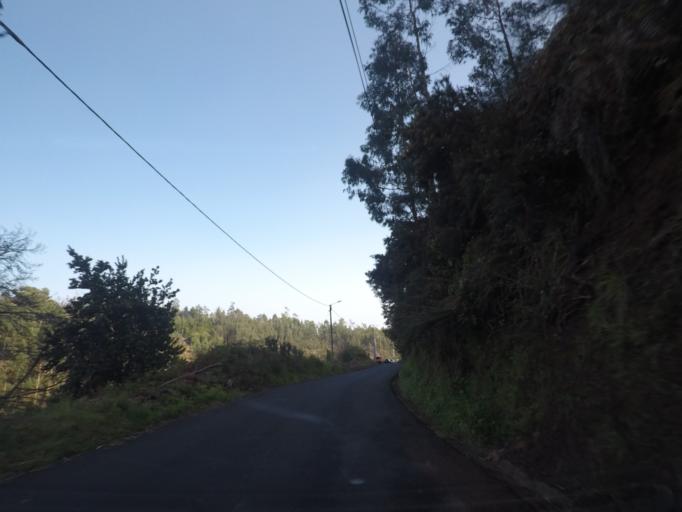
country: PT
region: Madeira
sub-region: Ribeira Brava
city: Campanario
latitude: 32.6766
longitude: -17.0067
